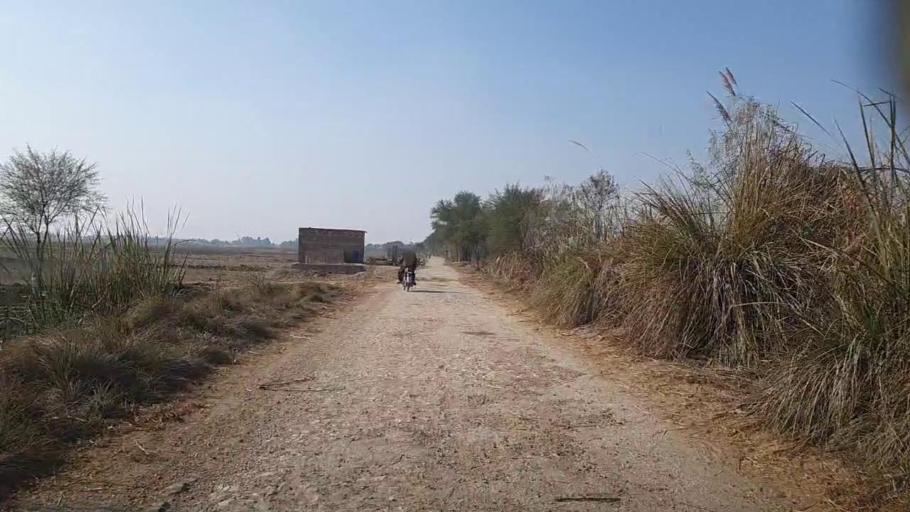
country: PK
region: Sindh
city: Mirpur Mathelo
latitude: 27.9014
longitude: 69.6359
